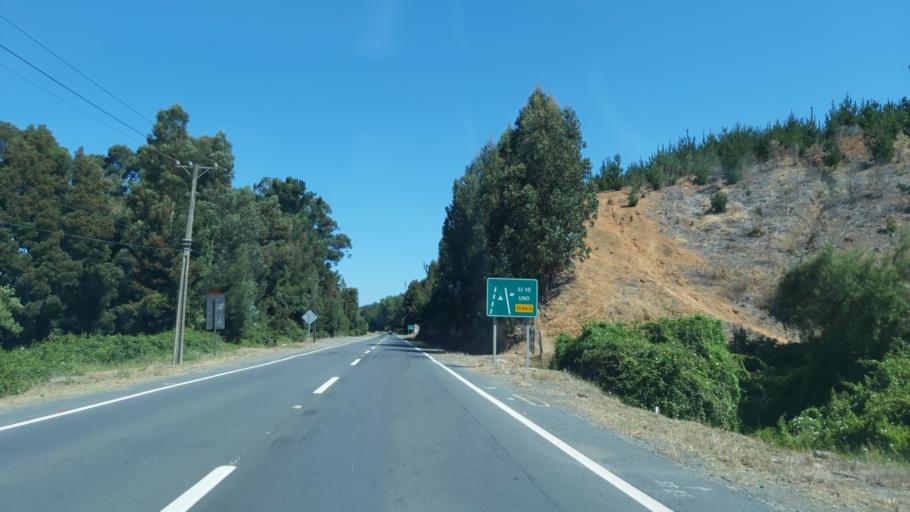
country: CL
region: Biobio
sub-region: Provincia de Concepcion
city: Chiguayante
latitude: -36.8955
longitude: -73.0587
